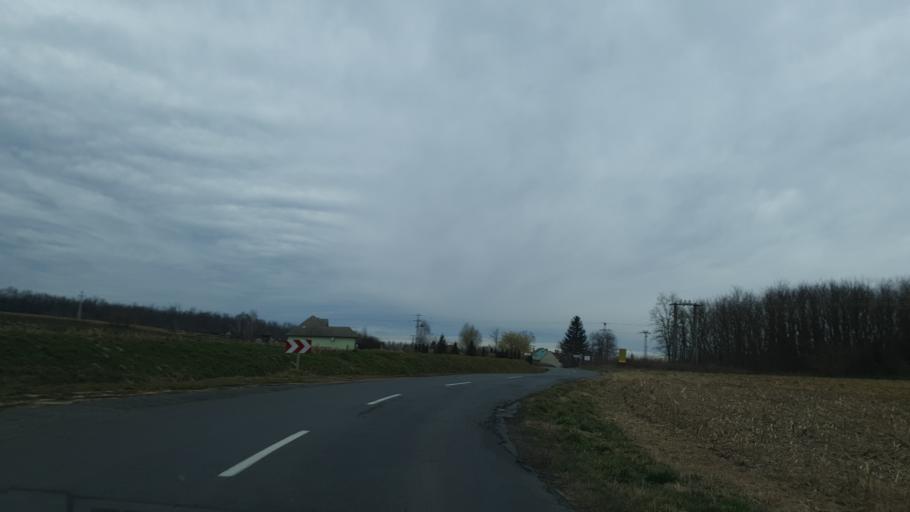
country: HU
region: Zala
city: Sarmellek
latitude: 46.7197
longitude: 17.1063
